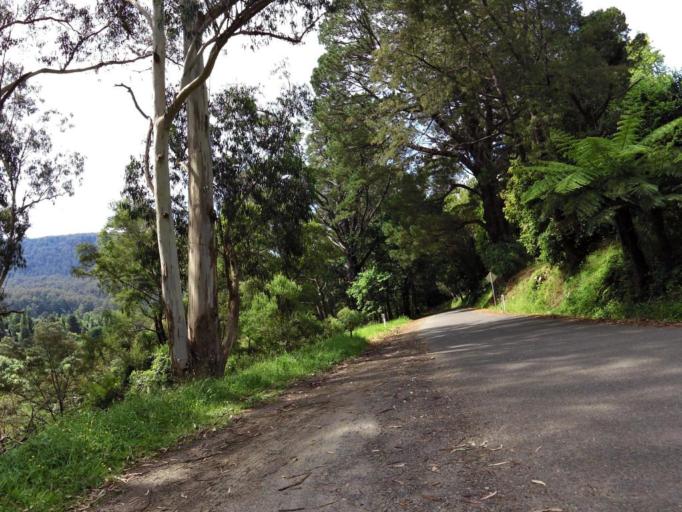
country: AU
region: Victoria
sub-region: Yarra Ranges
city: Millgrove
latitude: -37.7551
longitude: 145.7080
